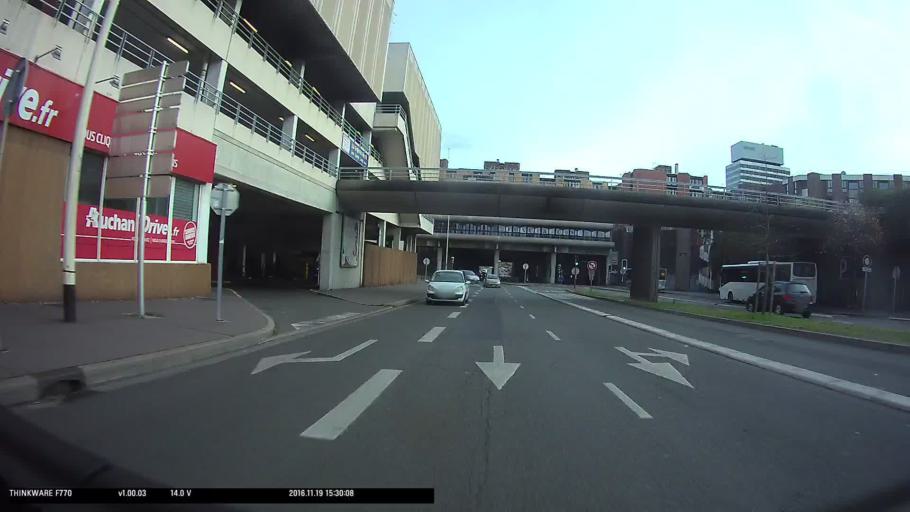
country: FR
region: Ile-de-France
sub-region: Departement du Val-d'Oise
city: Cergy-Pontoise
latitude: 49.0383
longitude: 2.0781
